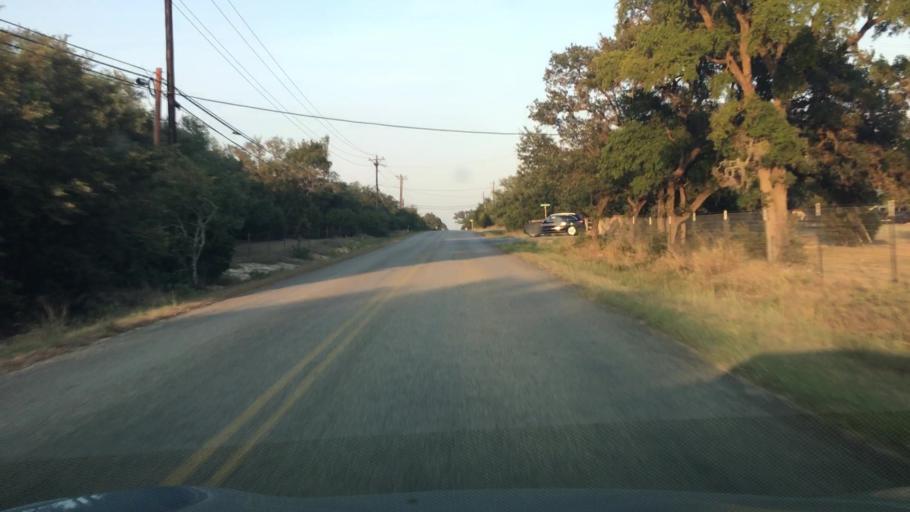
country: US
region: Texas
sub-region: Hays County
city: Dripping Springs
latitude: 30.1534
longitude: -98.0126
